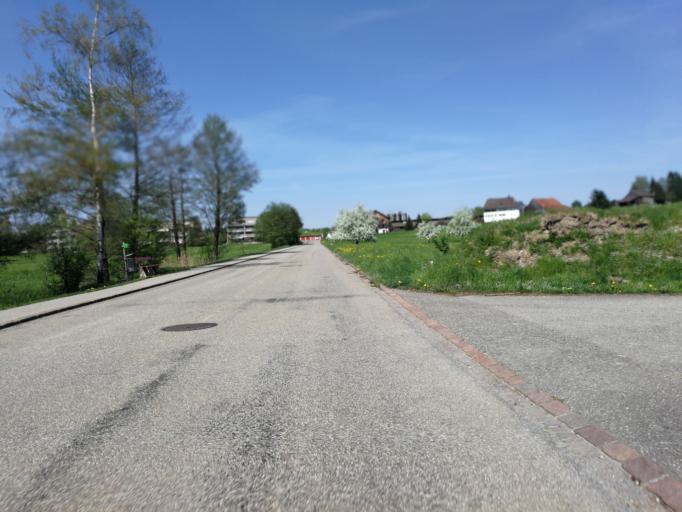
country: CH
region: Zurich
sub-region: Bezirk Hinwil
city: Bubikon
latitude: 47.2781
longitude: 8.8199
